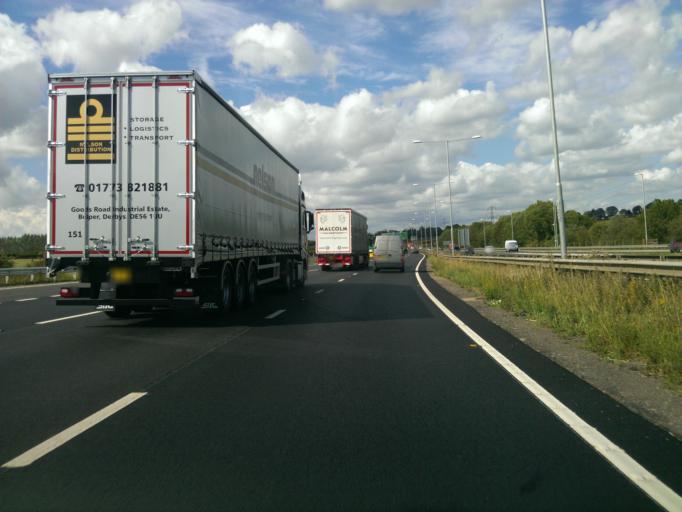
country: GB
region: England
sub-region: Northamptonshire
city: Kettering
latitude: 52.3929
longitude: -0.7501
